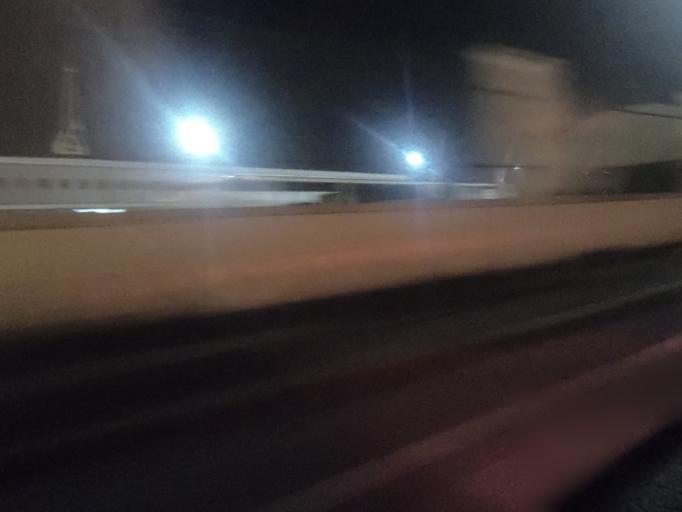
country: PT
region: Setubal
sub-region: Setubal
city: Setubal
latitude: 38.5199
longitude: -8.8799
